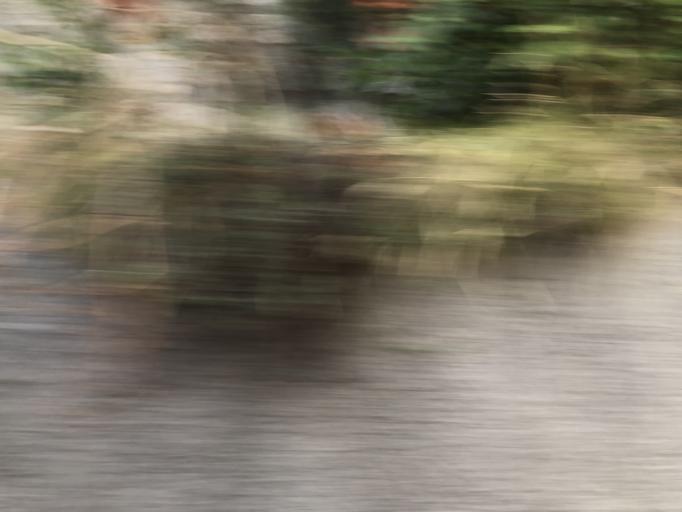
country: FR
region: Provence-Alpes-Cote d'Azur
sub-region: Departement des Alpes-Maritimes
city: Beaulieu-sur-Mer
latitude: 43.7093
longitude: 7.3232
